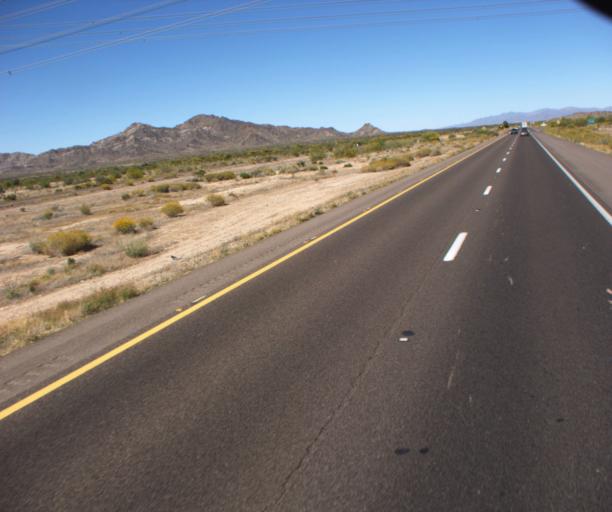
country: US
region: Arizona
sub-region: Maricopa County
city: Buckeye
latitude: 33.2280
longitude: -112.6421
